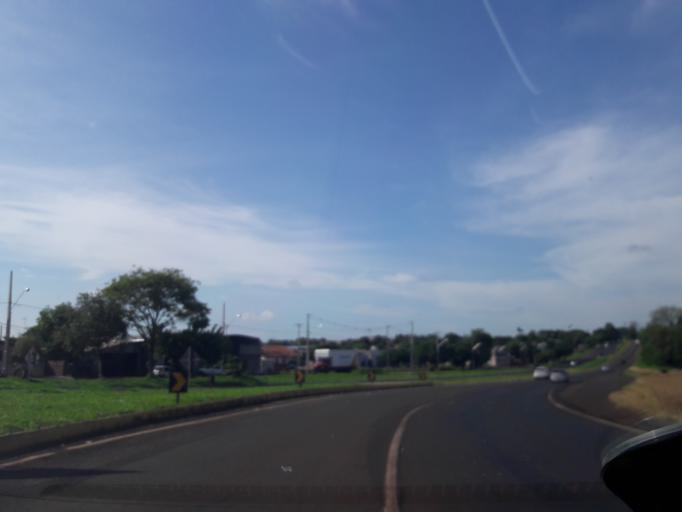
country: BR
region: Parana
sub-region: Paicandu
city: Paicandu
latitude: -23.6054
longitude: -52.0841
